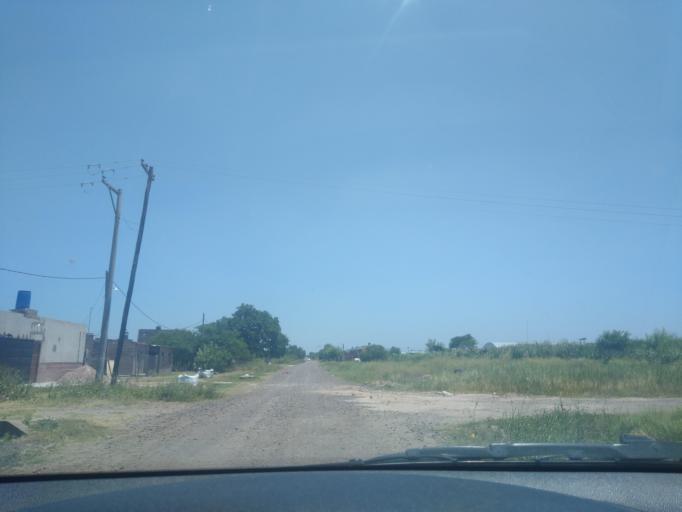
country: AR
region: Chaco
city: Puerto Tirol
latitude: -27.3825
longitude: -59.0919
